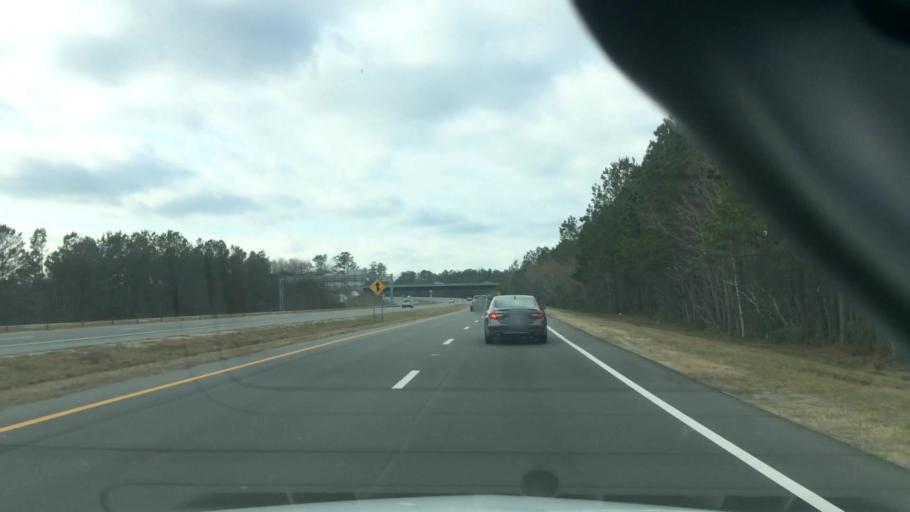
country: US
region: North Carolina
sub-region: New Hanover County
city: Skippers Corner
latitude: 34.3187
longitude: -77.8775
